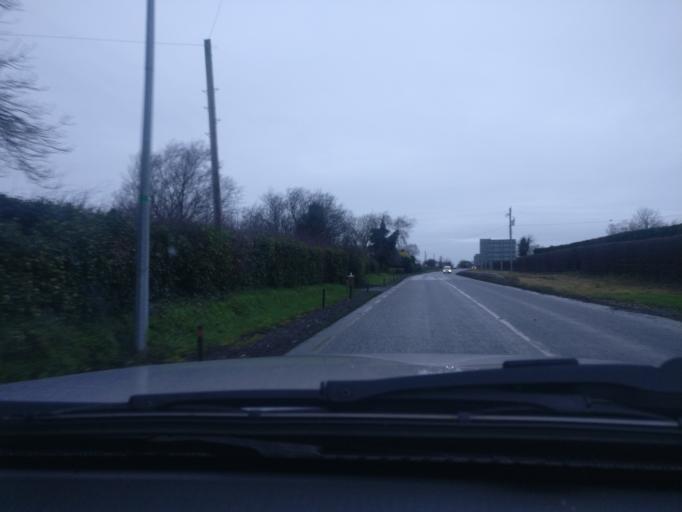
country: IE
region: Leinster
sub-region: An Mhi
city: Dunshaughlin
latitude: 53.5006
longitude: -6.5942
